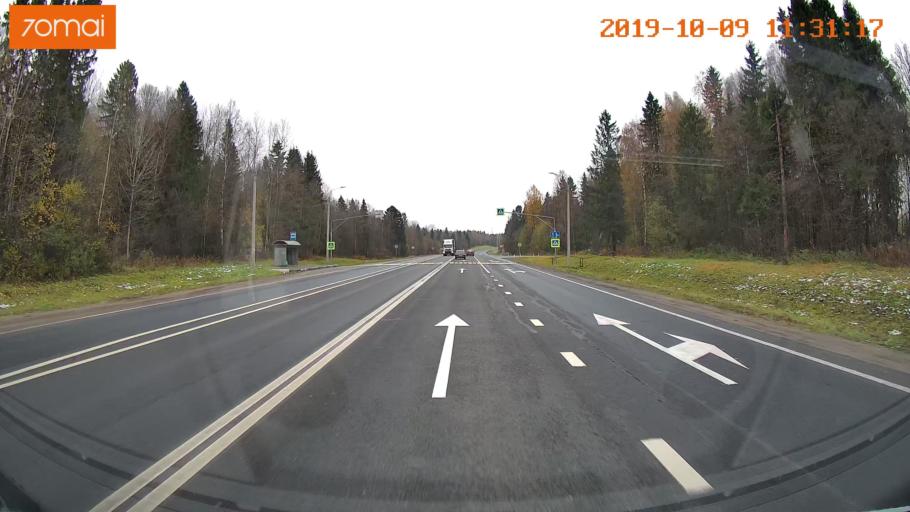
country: RU
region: Vologda
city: Gryazovets
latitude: 59.0469
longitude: 40.0927
